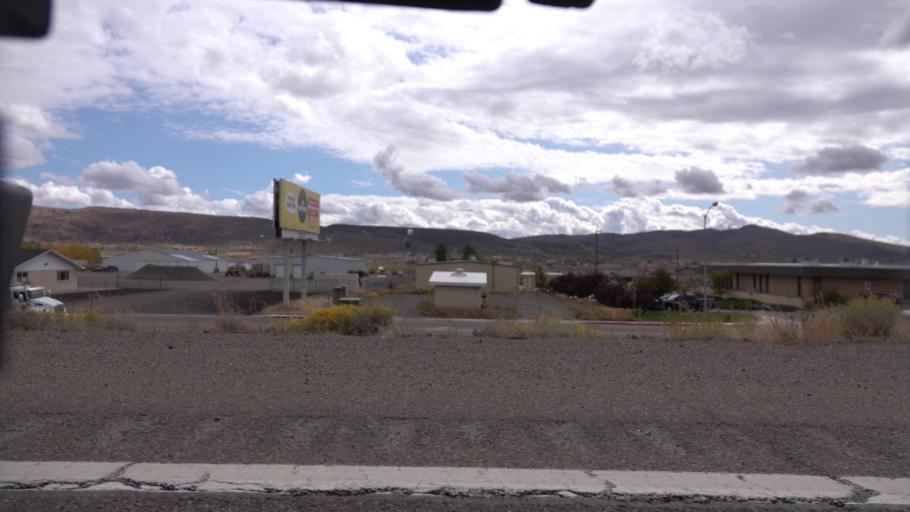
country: US
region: Nevada
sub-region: Elko County
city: Elko
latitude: 40.8649
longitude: -115.7335
